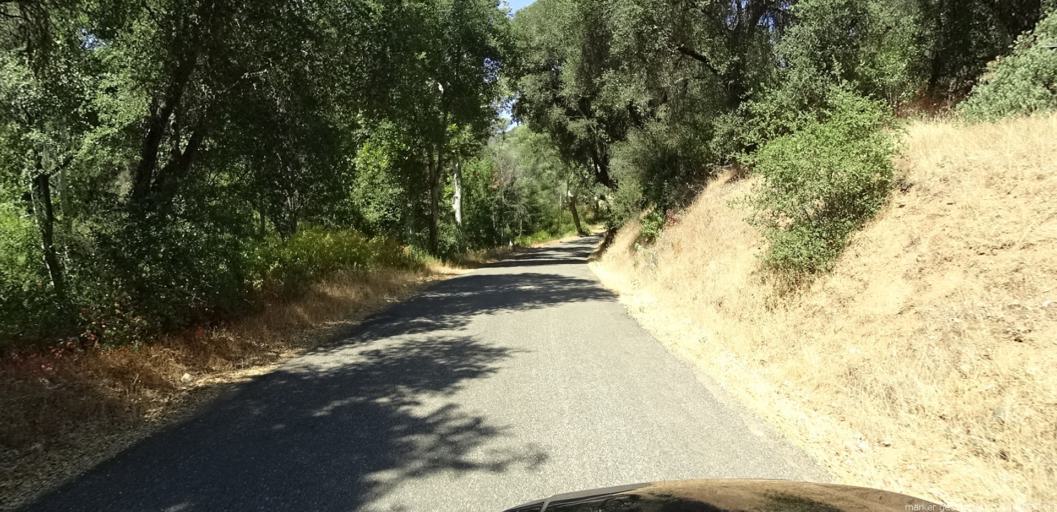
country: US
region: California
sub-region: Monterey County
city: King City
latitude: 36.0035
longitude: -121.3893
